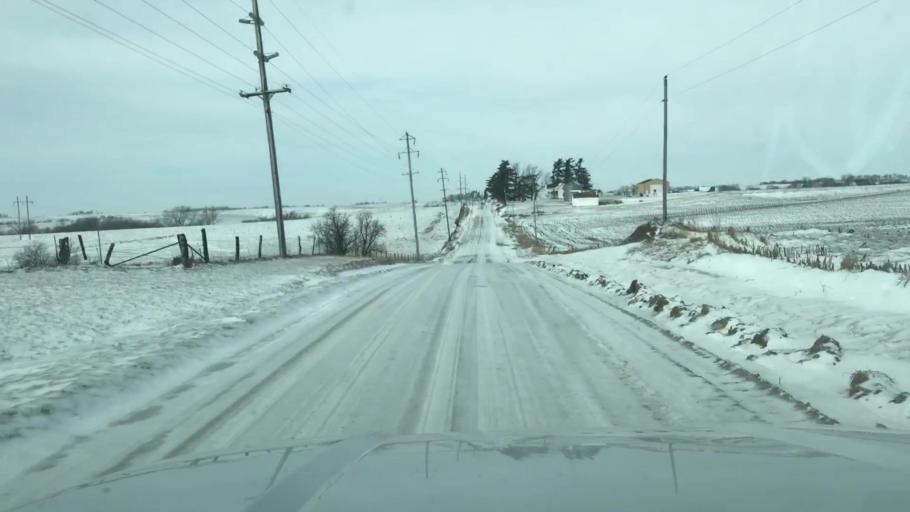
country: US
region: Missouri
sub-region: Holt County
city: Oregon
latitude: 40.1301
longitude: -95.0700
